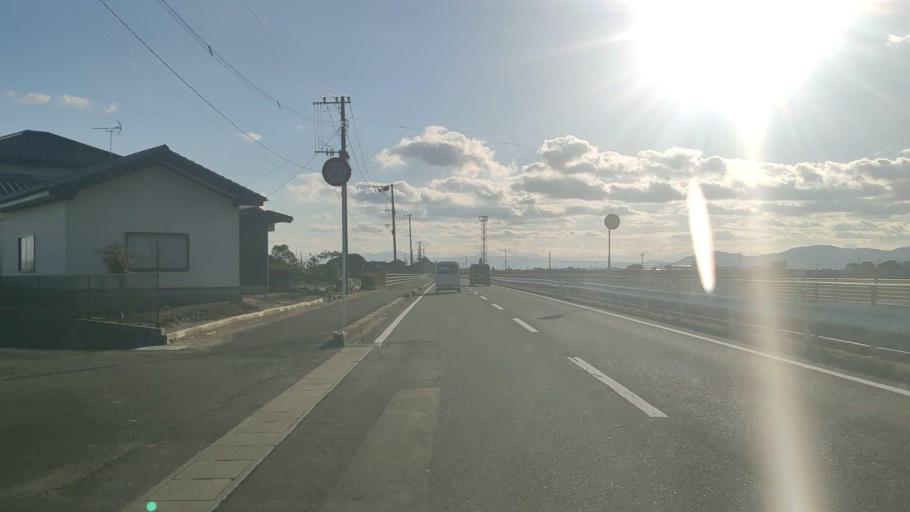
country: JP
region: Saga Prefecture
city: Saga-shi
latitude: 33.2903
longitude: 130.2352
